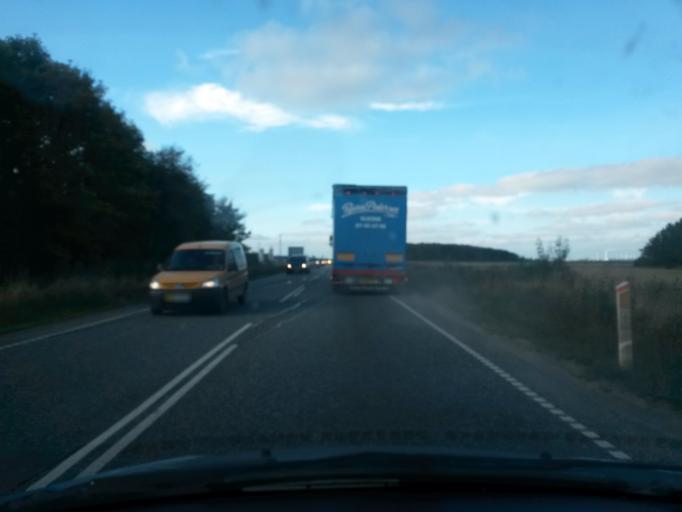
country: DK
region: Central Jutland
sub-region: Holstebro Kommune
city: Holstebro
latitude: 56.3353
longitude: 8.6479
